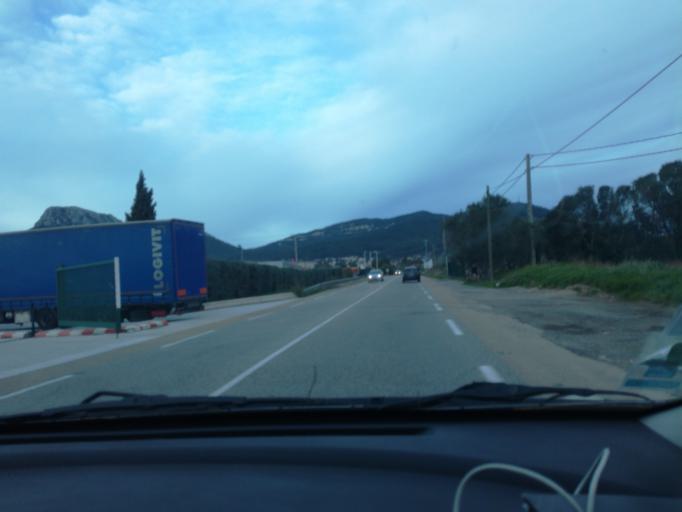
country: FR
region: Provence-Alpes-Cote d'Azur
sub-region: Departement du Var
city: La Crau
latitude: 43.1597
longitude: 6.0631
